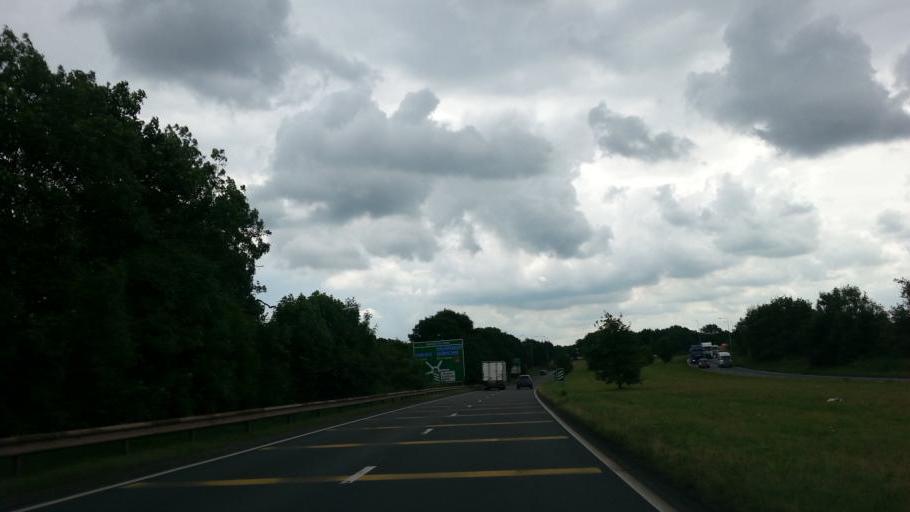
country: GB
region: England
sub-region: City and Borough of Birmingham
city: Sutton Coldfield
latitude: 52.5935
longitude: -1.7875
